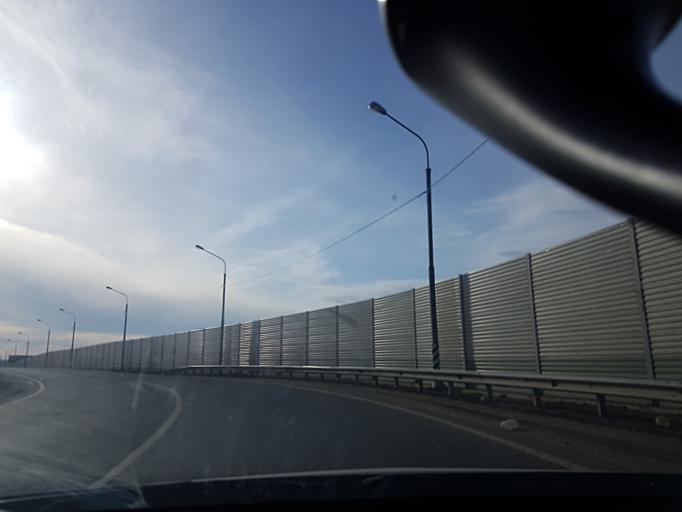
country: RU
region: Moskovskaya
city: Rozhdestveno
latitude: 55.8117
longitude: 37.0348
